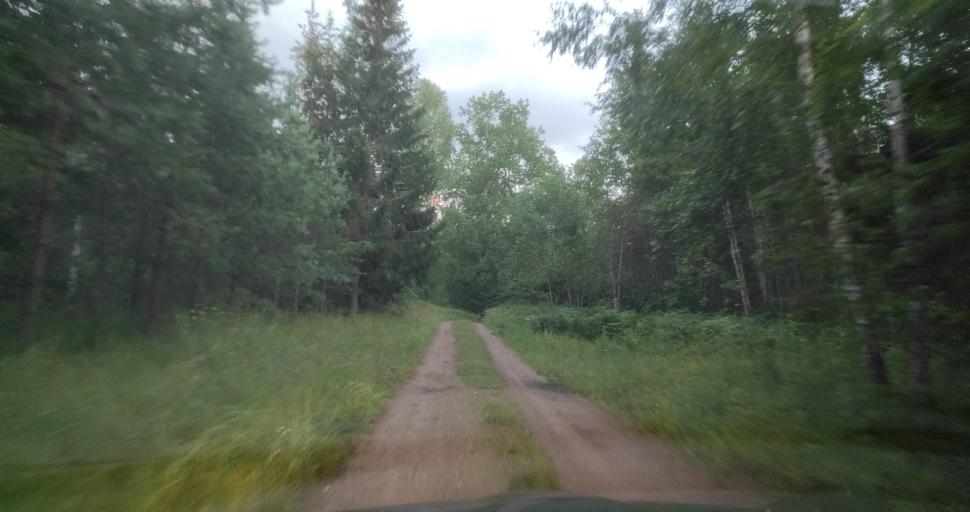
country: LV
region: Kuldigas Rajons
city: Kuldiga
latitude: 57.0631
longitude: 21.8650
